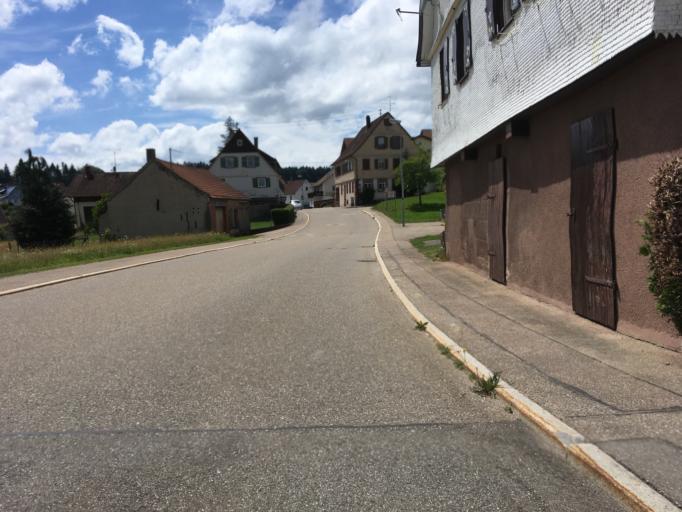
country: DE
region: Baden-Wuerttemberg
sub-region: Karlsruhe Region
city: Enzklosterle
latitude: 48.5953
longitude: 8.4211
